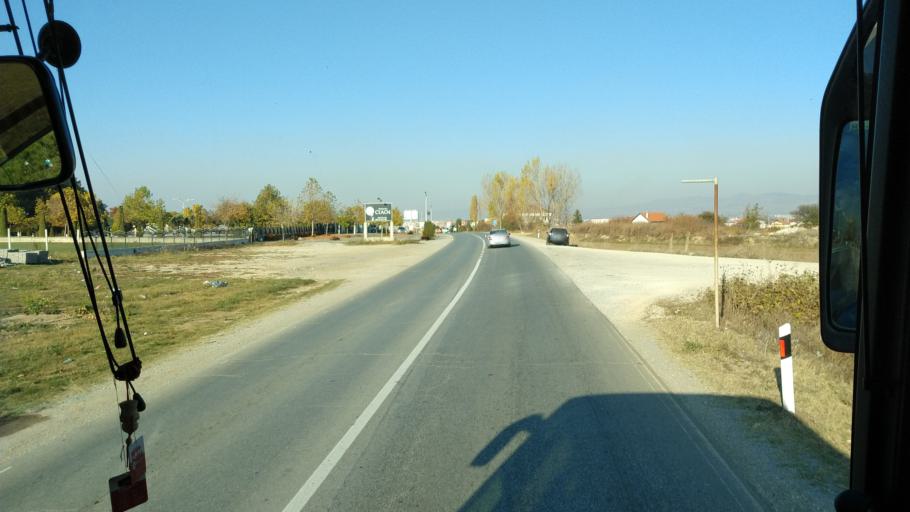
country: XK
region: Pristina
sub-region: Lipjan
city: Lipljan
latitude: 42.4998
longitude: 21.1073
